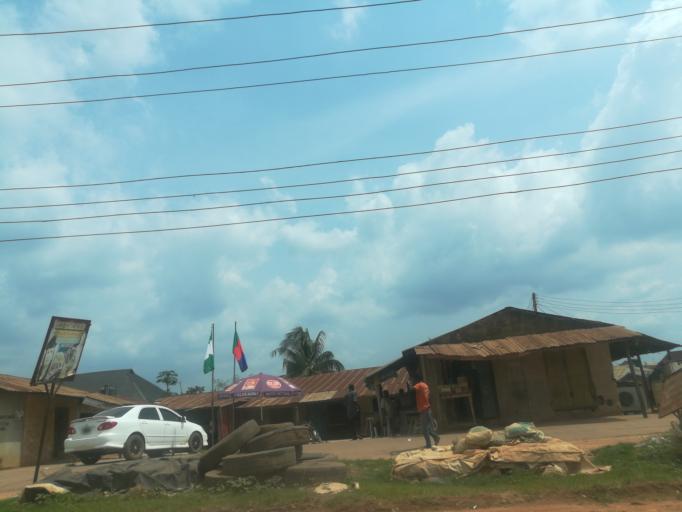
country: NG
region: Oyo
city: Moniya
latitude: 7.4599
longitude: 3.9537
